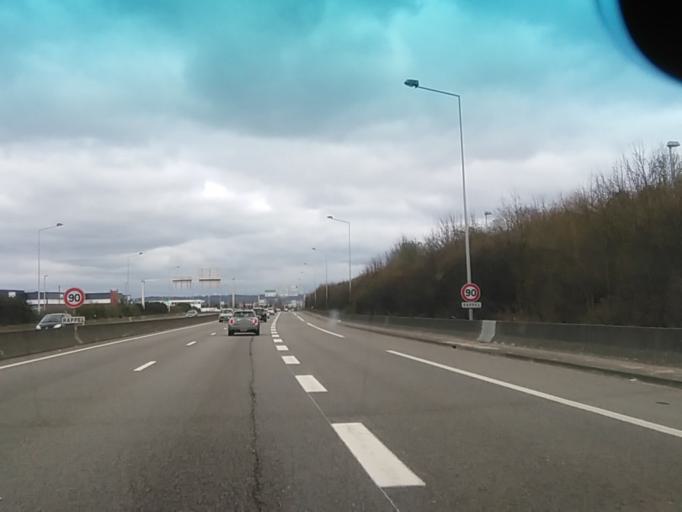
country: FR
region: Haute-Normandie
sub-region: Departement de la Seine-Maritime
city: Le Grand-Quevilly
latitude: 49.4034
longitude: 1.0340
